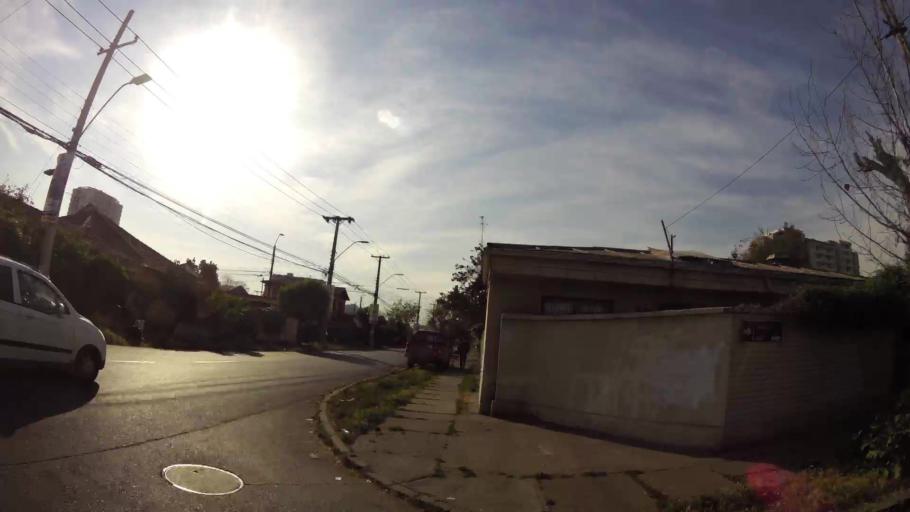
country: CL
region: Santiago Metropolitan
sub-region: Provincia de Santiago
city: Santiago
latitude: -33.5138
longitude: -70.6667
